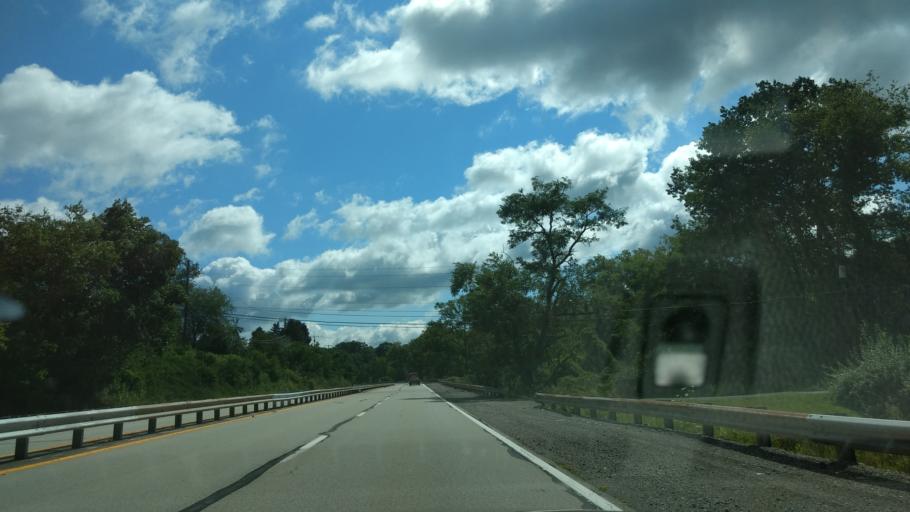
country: US
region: Pennsylvania
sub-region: Westmoreland County
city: Murrysville
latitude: 40.5110
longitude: -79.6517
